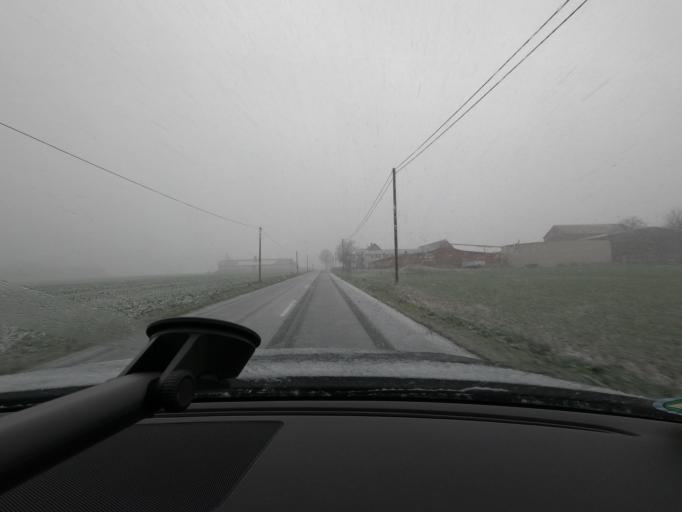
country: DE
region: North Rhine-Westphalia
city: Marsberg
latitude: 51.5352
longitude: 8.8410
